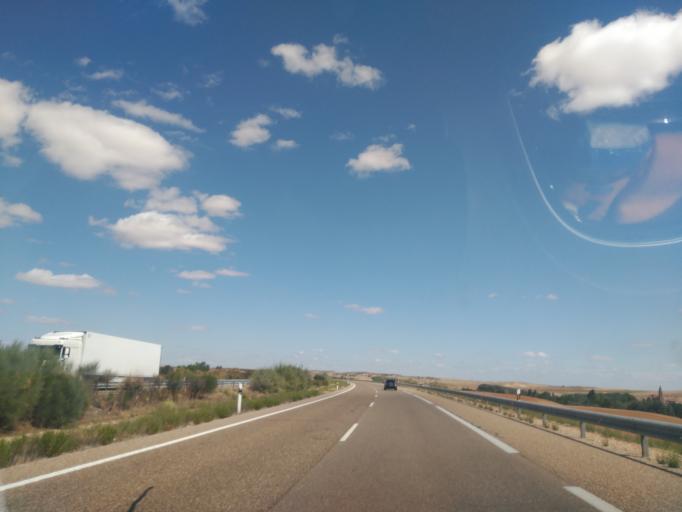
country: ES
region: Castille and Leon
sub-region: Provincia de Zamora
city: Canizal
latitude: 41.1669
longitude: -5.3847
